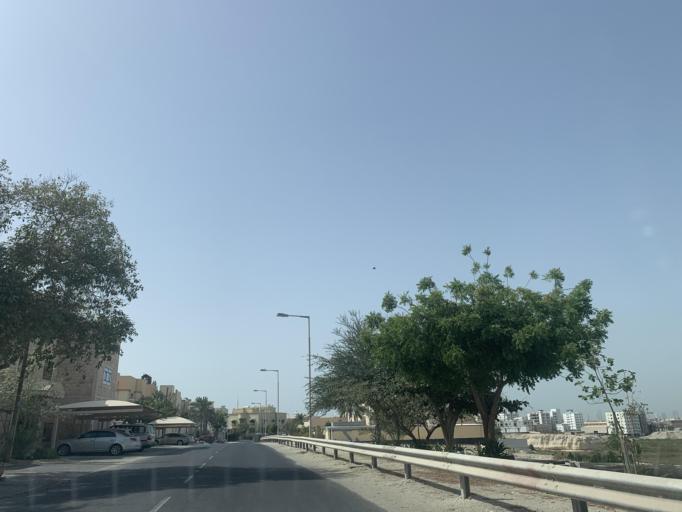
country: BH
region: Northern
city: Ar Rifa'
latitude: 26.1435
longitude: 50.5701
